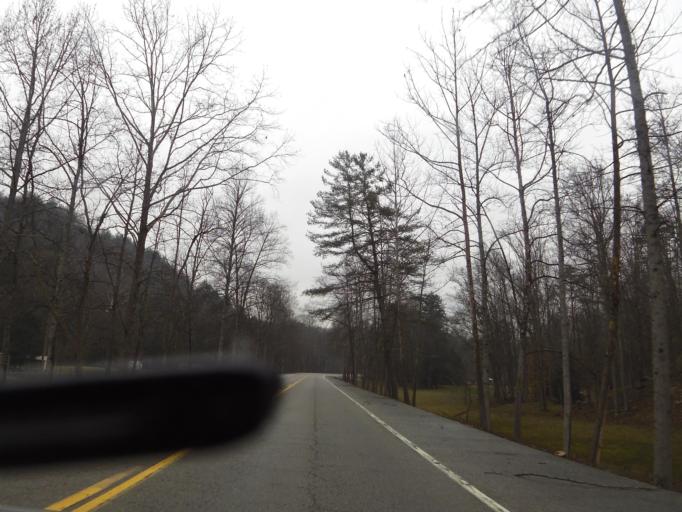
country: US
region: Tennessee
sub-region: Roane County
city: Harriman
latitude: 36.0023
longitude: -84.5104
